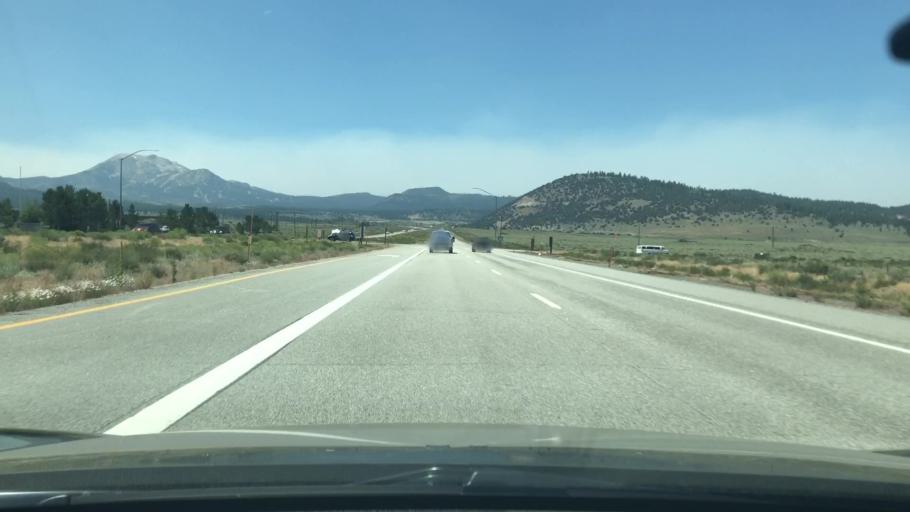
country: US
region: California
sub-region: Mono County
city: Mammoth Lakes
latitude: 37.6293
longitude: -118.8629
